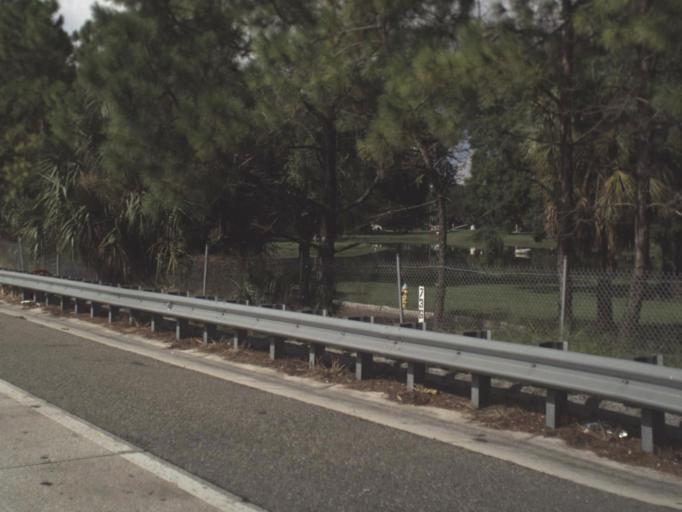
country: US
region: Florida
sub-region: Hillsborough County
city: Tampa
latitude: 27.9747
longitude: -82.4537
